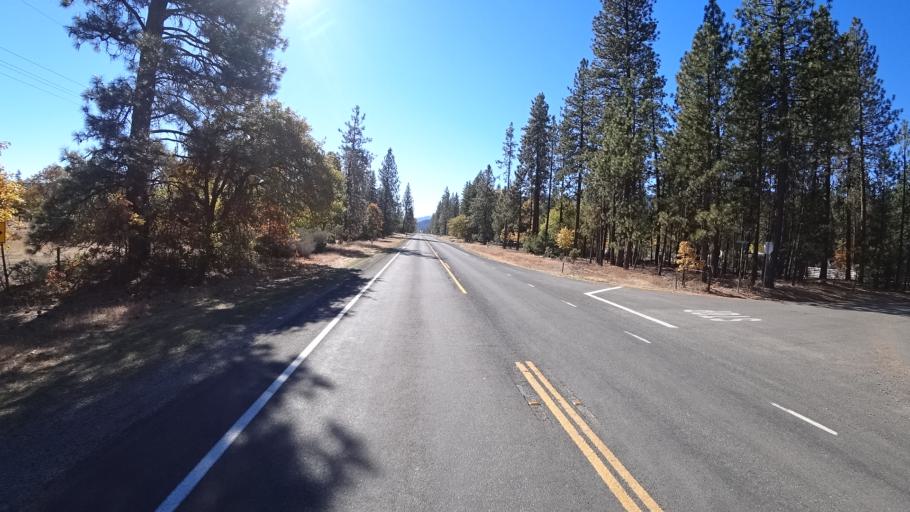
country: US
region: California
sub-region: Siskiyou County
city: Yreka
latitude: 41.5138
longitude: -122.9067
